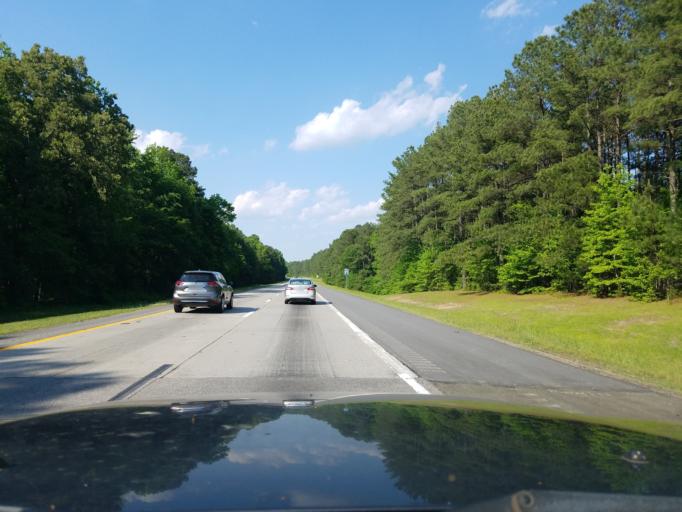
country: US
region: North Carolina
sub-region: Granville County
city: Butner
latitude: 36.1537
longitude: -78.7189
